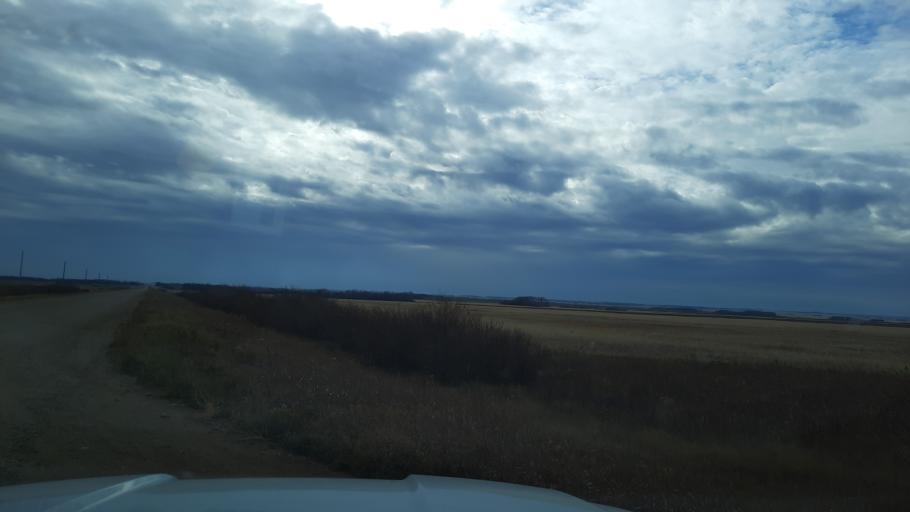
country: CA
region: Saskatchewan
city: Pilot Butte
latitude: 50.7554
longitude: -104.2700
